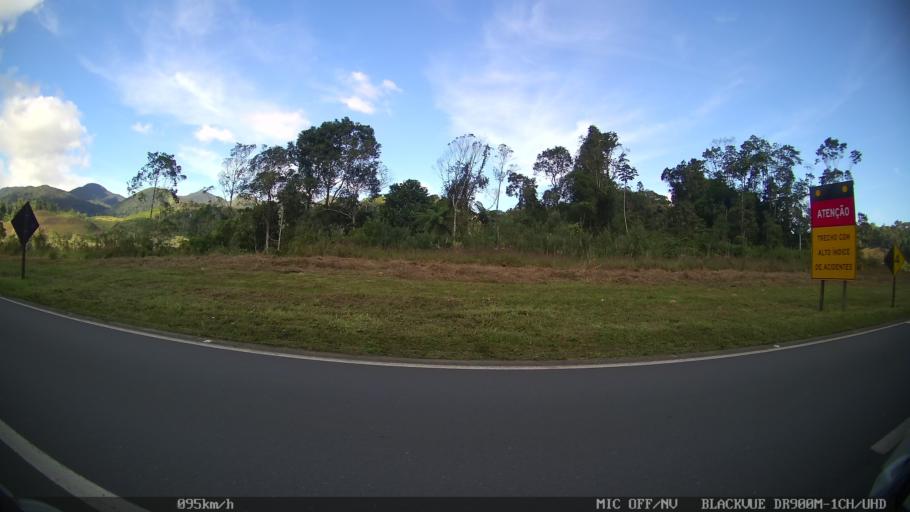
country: BR
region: Sao Paulo
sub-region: Cajati
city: Cajati
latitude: -24.9040
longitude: -48.2526
